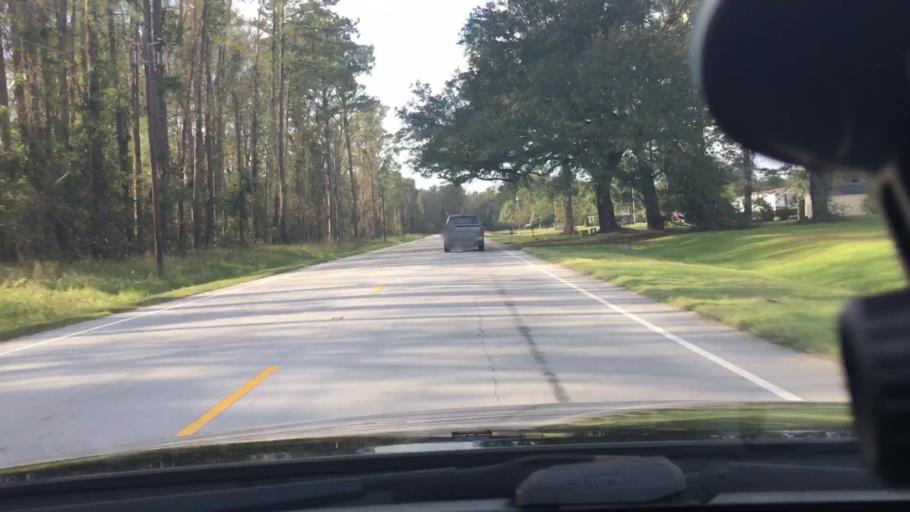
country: US
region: North Carolina
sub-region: Craven County
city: Vanceboro
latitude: 35.2258
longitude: -77.0698
